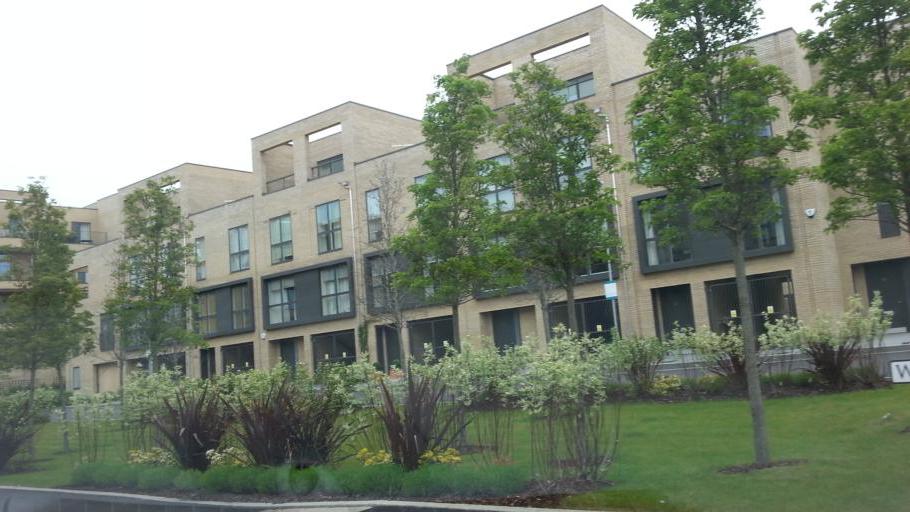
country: GB
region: England
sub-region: Cambridgeshire
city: Cambridge
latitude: 52.1783
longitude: 0.1243
